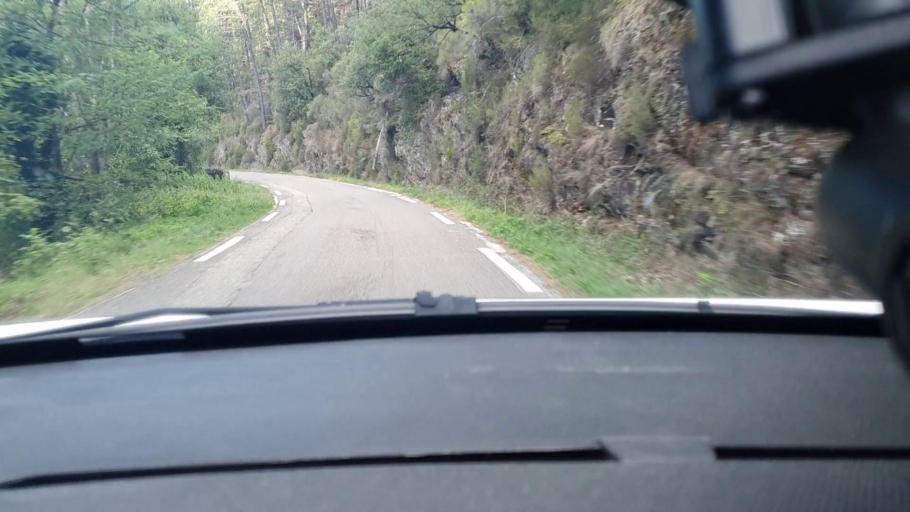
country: FR
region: Languedoc-Roussillon
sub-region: Departement du Gard
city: Besseges
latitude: 44.3659
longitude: 3.9976
